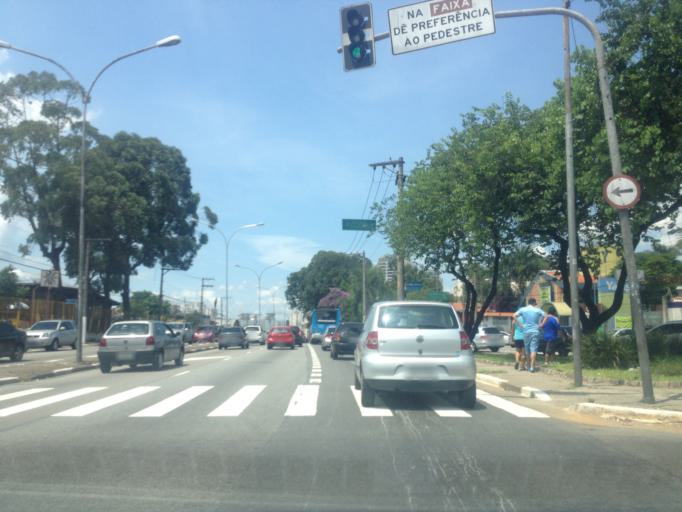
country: BR
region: Sao Paulo
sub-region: Diadema
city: Diadema
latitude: -23.6534
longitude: -46.6800
